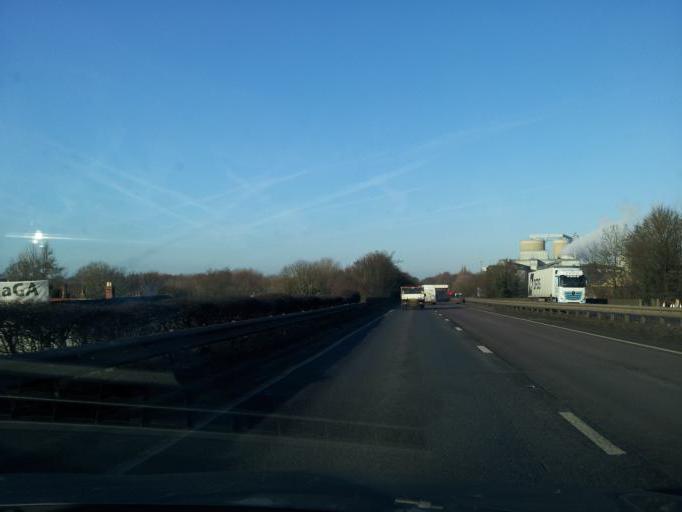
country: GB
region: England
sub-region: Suffolk
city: Bury St Edmunds
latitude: 52.2473
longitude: 0.7243
